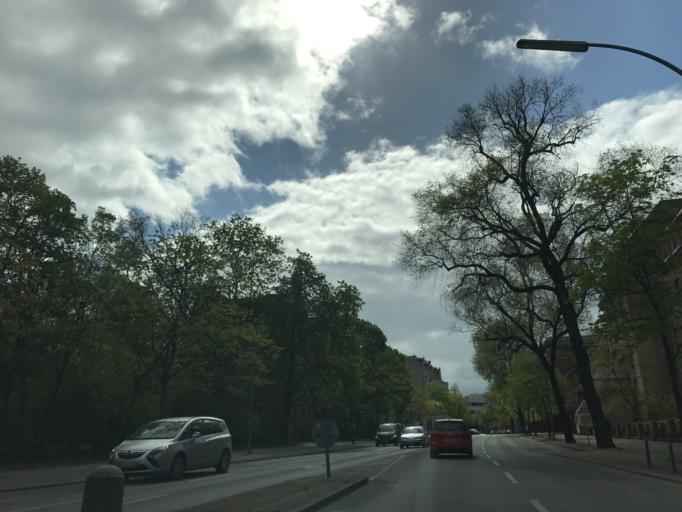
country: DE
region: Berlin
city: Tiergarten Bezirk
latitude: 52.5266
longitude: 13.3553
